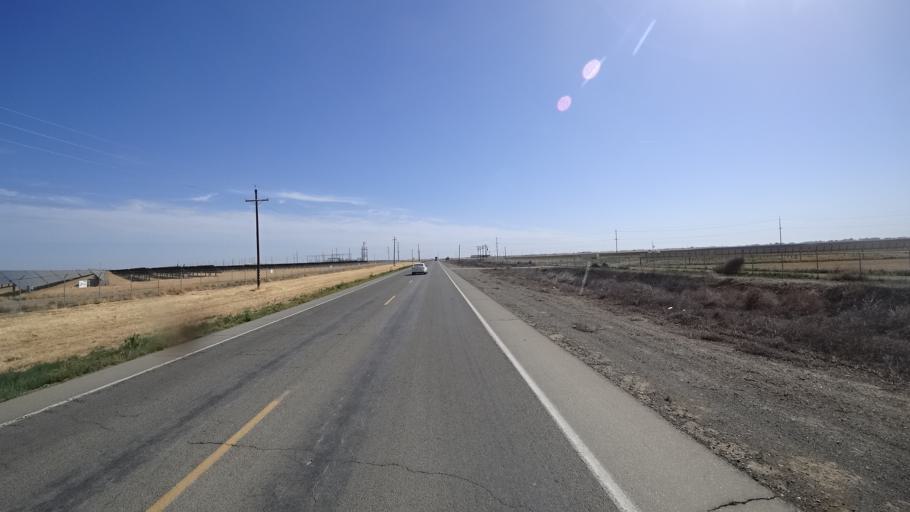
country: US
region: California
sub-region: Kings County
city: Lemoore Station
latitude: 36.2183
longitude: -119.9085
